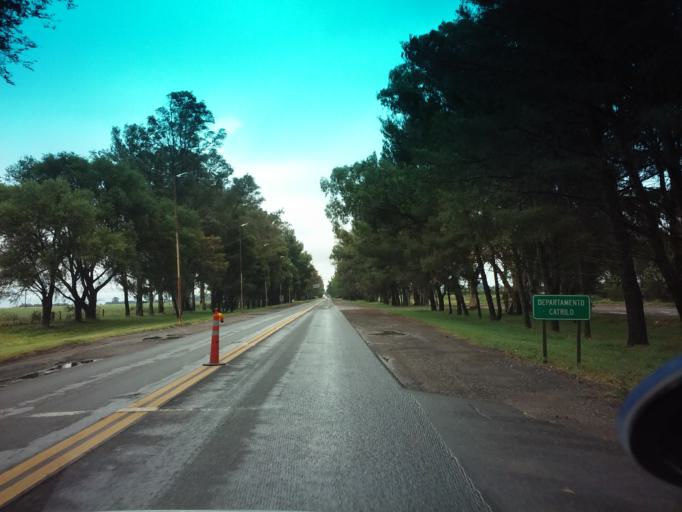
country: AR
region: La Pampa
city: Catrilo
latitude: -36.4107
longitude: -63.3874
